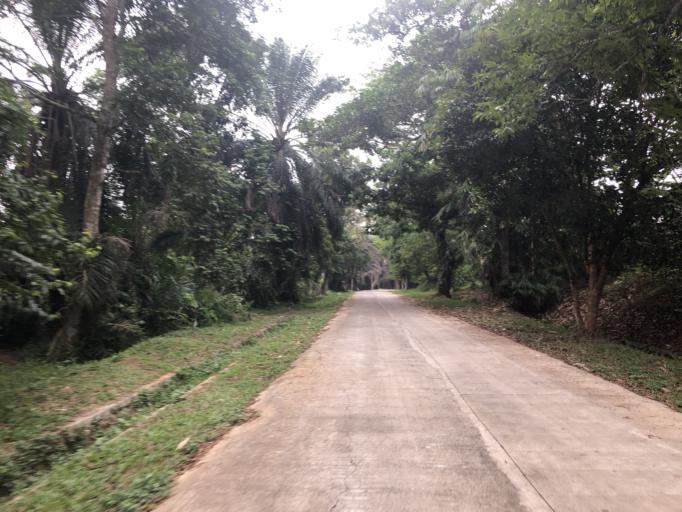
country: ID
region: West Java
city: Ciampea
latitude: -6.5513
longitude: 106.7136
